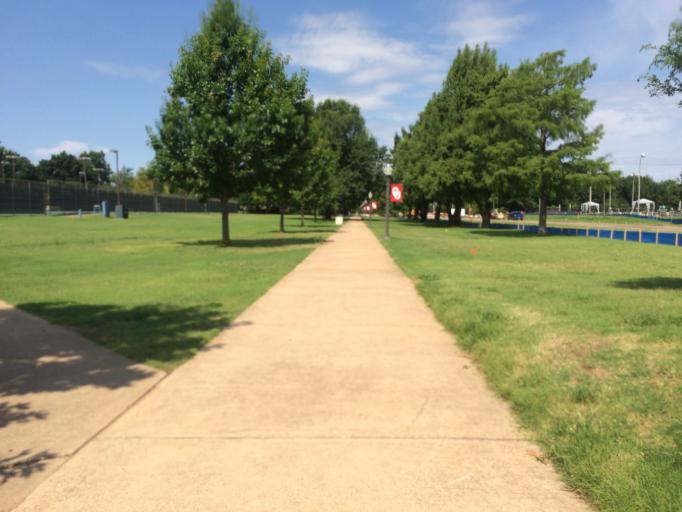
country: US
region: Oklahoma
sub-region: Cleveland County
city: Norman
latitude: 35.1964
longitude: -97.4420
